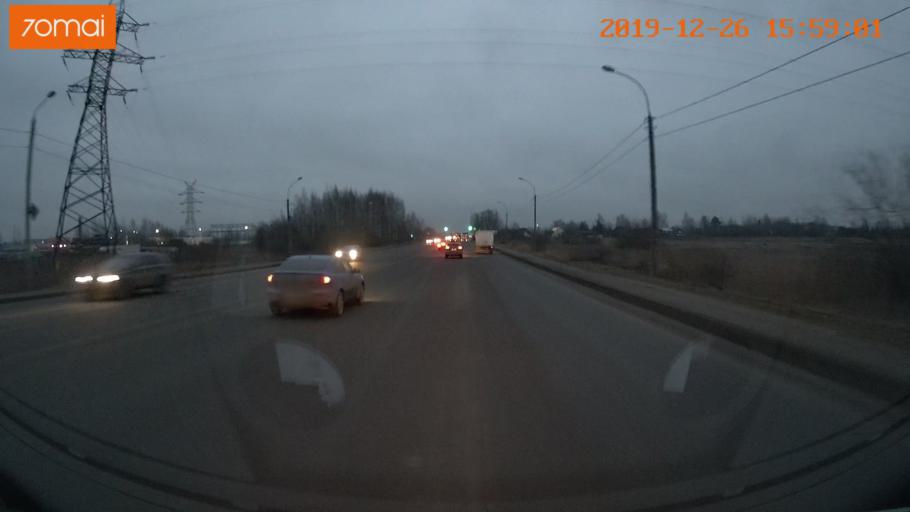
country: RU
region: Jaroslavl
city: Rybinsk
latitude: 58.0346
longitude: 38.8008
